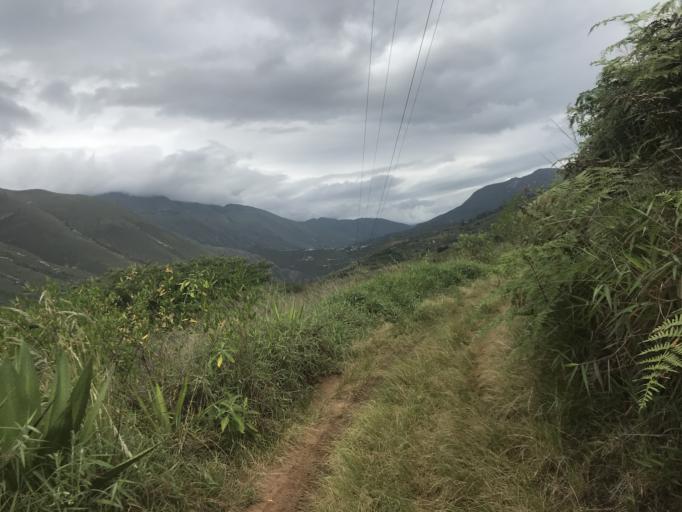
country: PE
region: Amazonas
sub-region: Provincia de Chachapoyas
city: Magdalena
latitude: -6.4015
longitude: -77.8847
